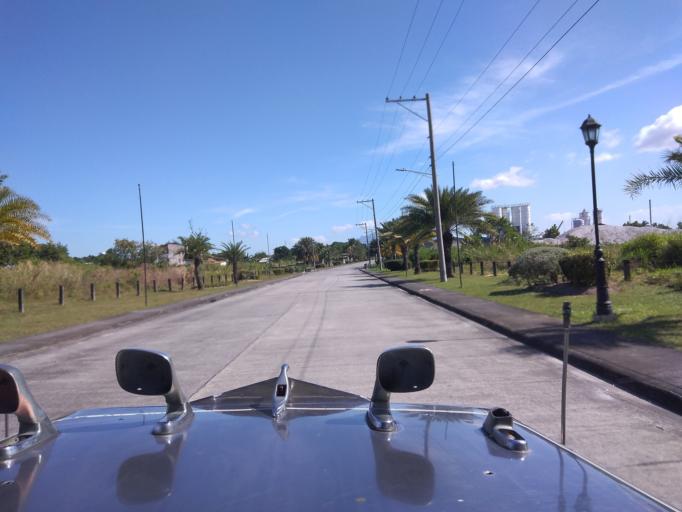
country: PH
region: Central Luzon
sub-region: Province of Pampanga
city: Calibutbut
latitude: 15.1051
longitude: 120.6022
